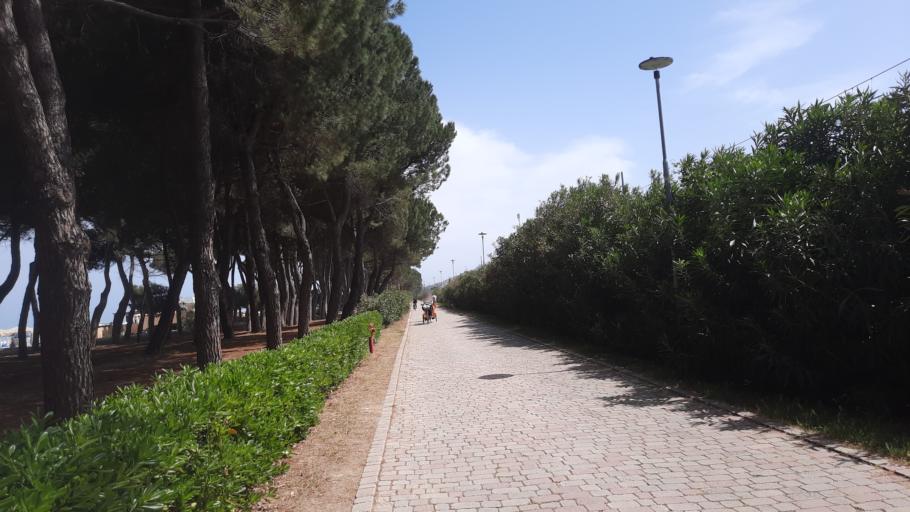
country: IT
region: Abruzzo
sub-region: Provincia di Teramo
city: Pineto
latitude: 42.6090
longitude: 14.0684
